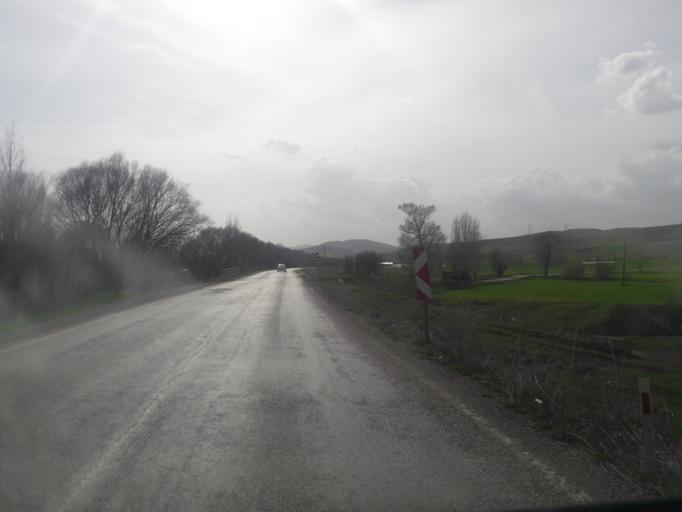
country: TR
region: Gumushane
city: Kelkit
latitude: 40.1427
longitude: 39.4240
